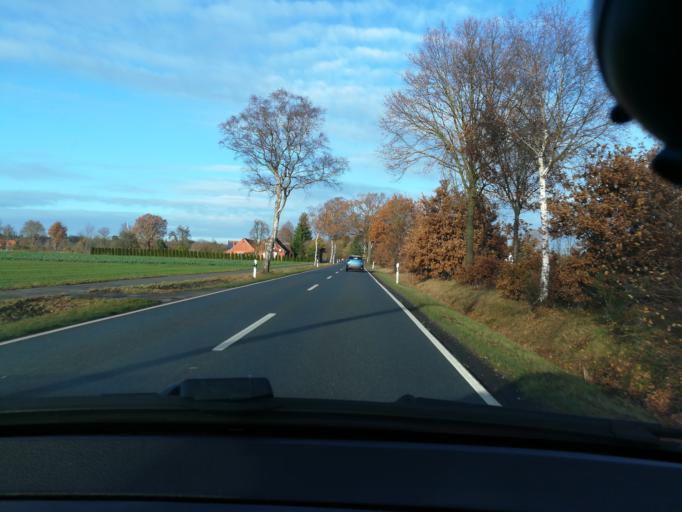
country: DE
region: Lower Saxony
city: Schwaforden
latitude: 52.7319
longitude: 8.8167
